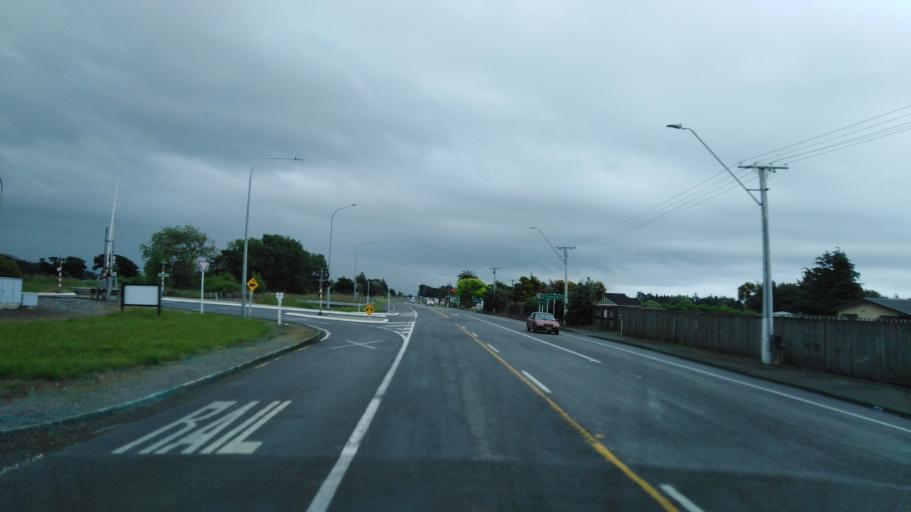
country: NZ
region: Manawatu-Wanganui
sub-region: Horowhenua District
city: Levin
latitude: -40.6475
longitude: 175.2609
